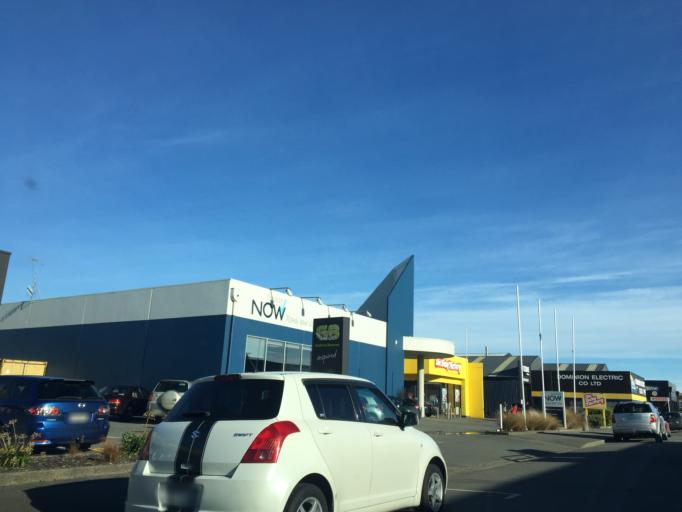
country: NZ
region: Southland
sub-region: Invercargill City
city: Invercargill
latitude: -46.4086
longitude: 168.3534
